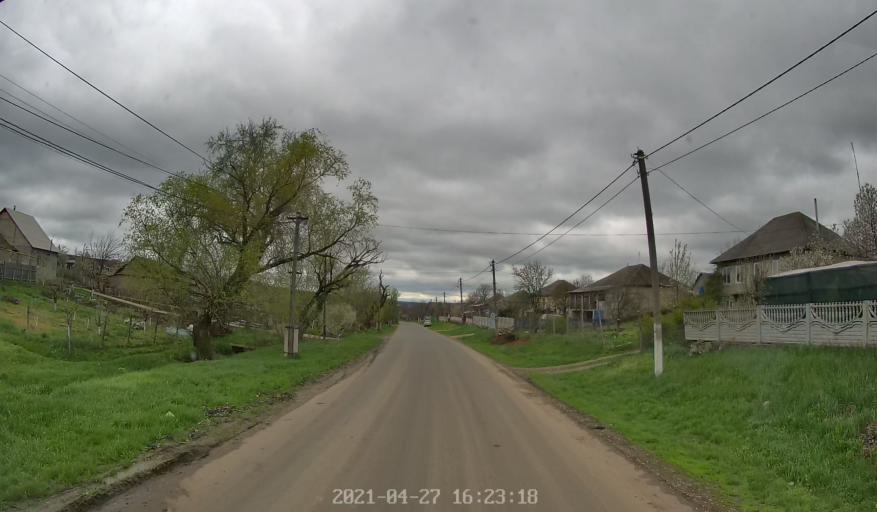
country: MD
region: Chisinau
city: Singera
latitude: 46.9997
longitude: 29.0171
